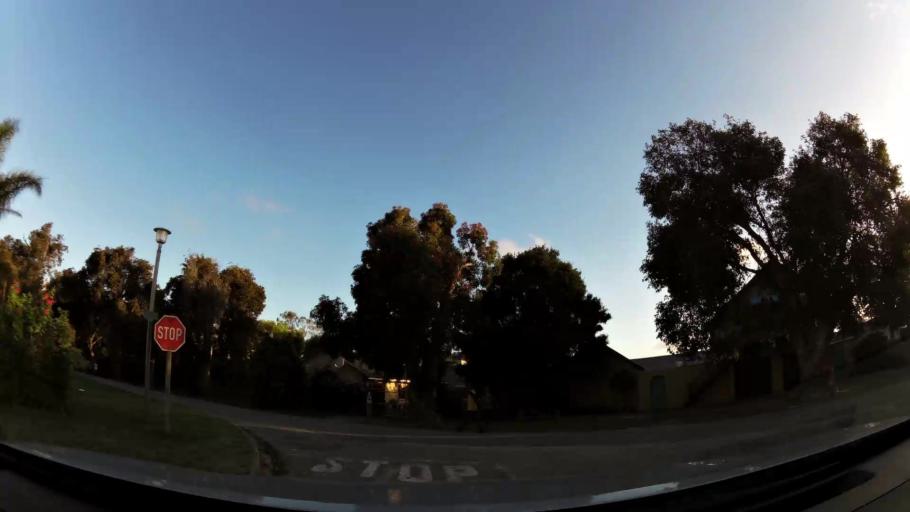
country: ZA
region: Western Cape
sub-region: Eden District Municipality
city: Knysna
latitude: -34.0164
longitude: 22.8028
